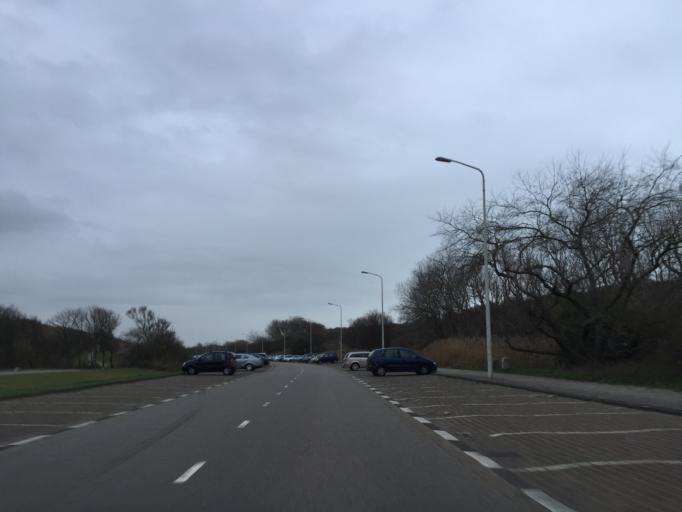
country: NL
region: South Holland
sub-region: Gemeente Westland
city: Poeldijk
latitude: 52.0632
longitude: 4.2163
